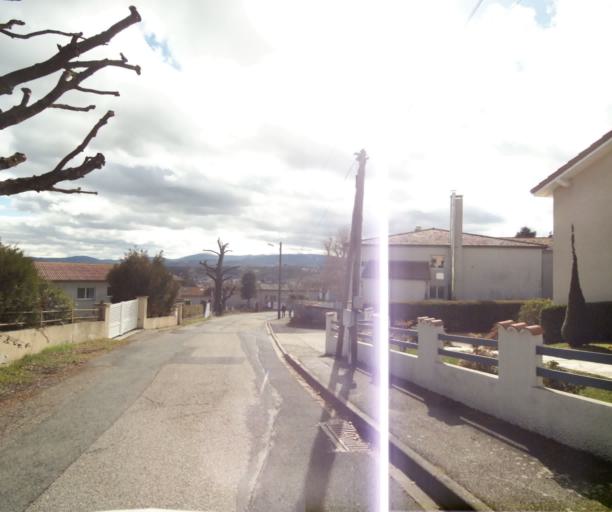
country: FR
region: Rhone-Alpes
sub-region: Departement de la Loire
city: La Talaudiere
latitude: 45.4875
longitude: 4.4284
